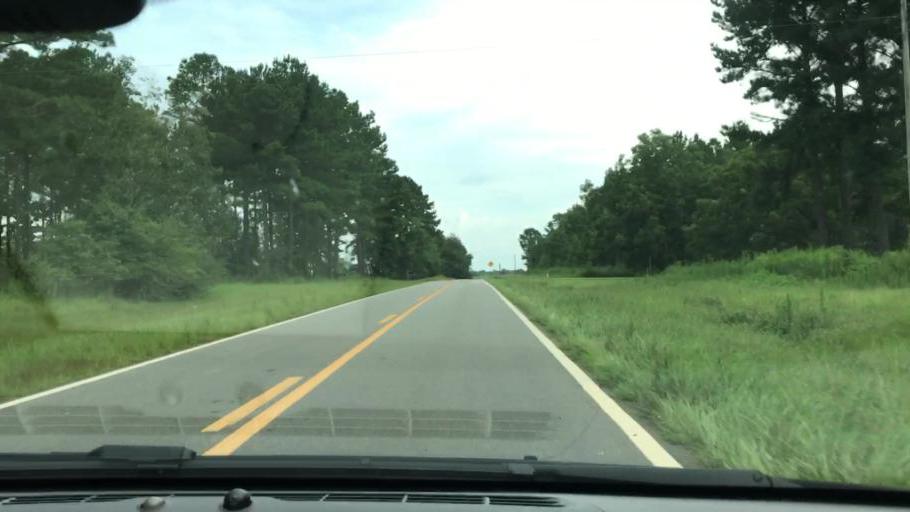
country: US
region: Georgia
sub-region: Early County
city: Blakely
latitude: 31.4549
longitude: -84.9152
